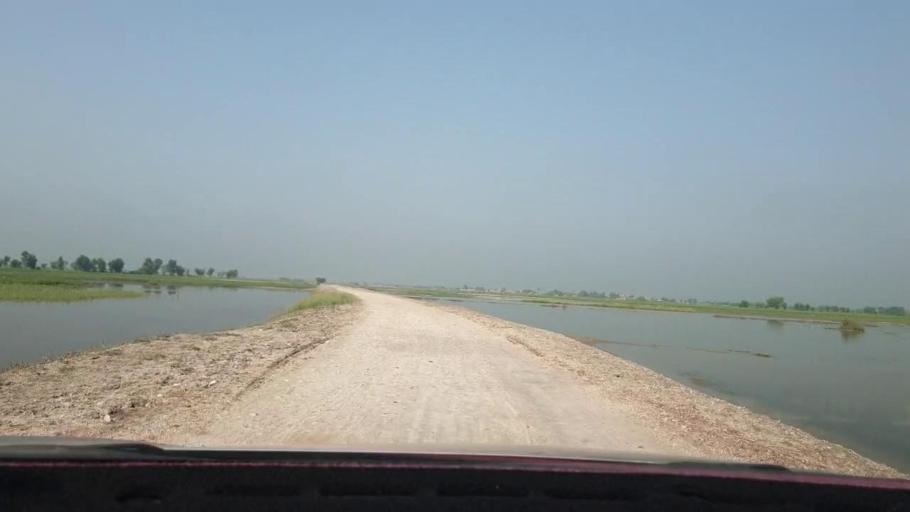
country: PK
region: Sindh
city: Nasirabad
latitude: 27.4383
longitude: 67.9758
